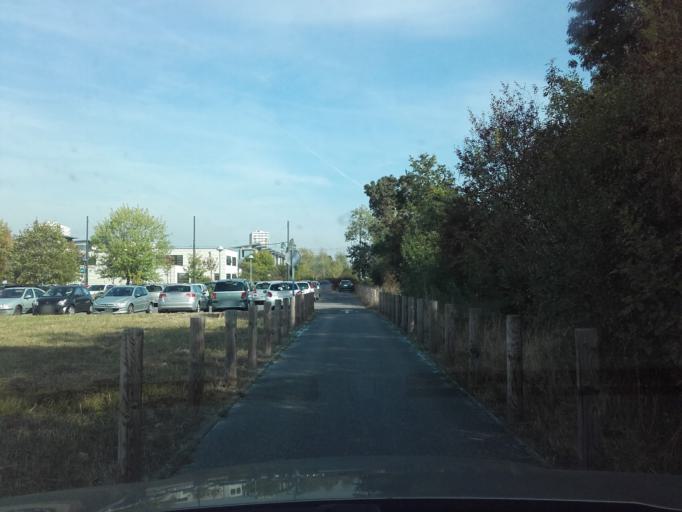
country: FR
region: Centre
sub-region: Departement d'Indre-et-Loire
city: Tours
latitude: 47.3670
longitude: 0.6866
